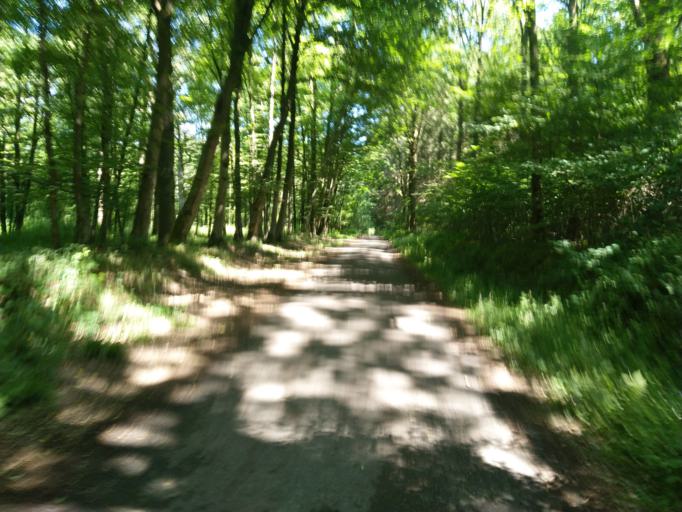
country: BE
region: Wallonia
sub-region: Province du Hainaut
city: Colfontaine
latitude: 50.3853
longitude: 3.8501
